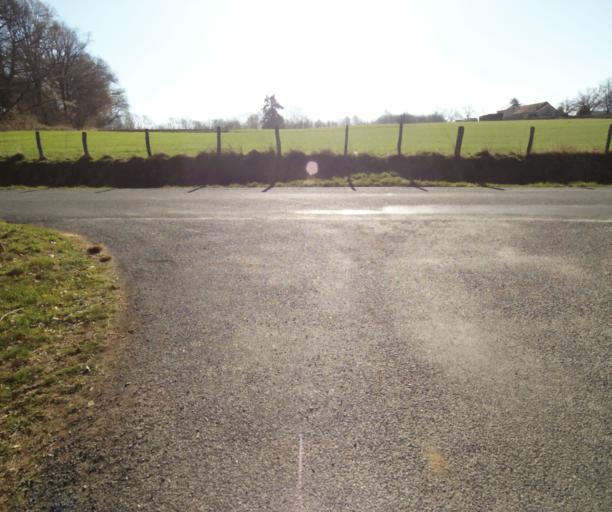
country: FR
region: Limousin
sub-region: Departement de la Correze
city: Saint-Clement
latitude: 45.3736
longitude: 1.6638
